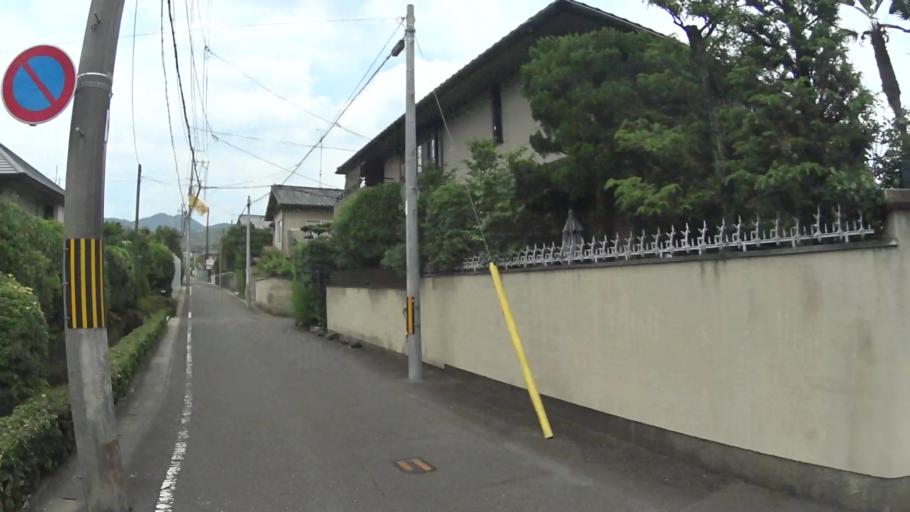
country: JP
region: Kyoto
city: Kyoto
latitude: 35.0238
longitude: 135.7099
